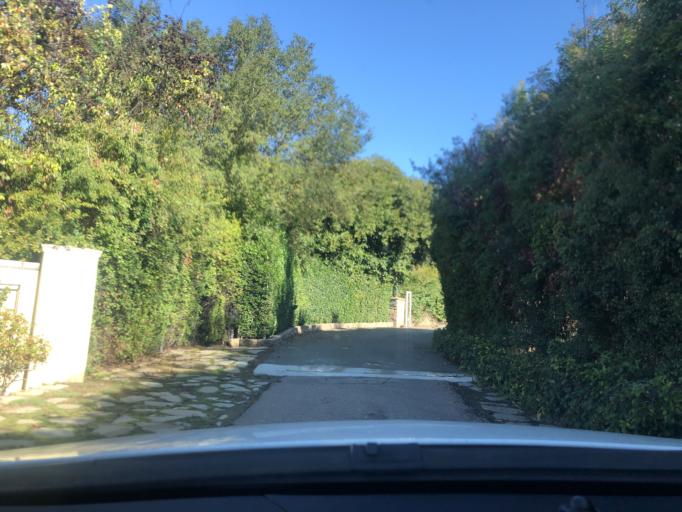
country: US
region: California
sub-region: San Diego County
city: El Cajon
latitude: 32.7768
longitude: -116.9397
